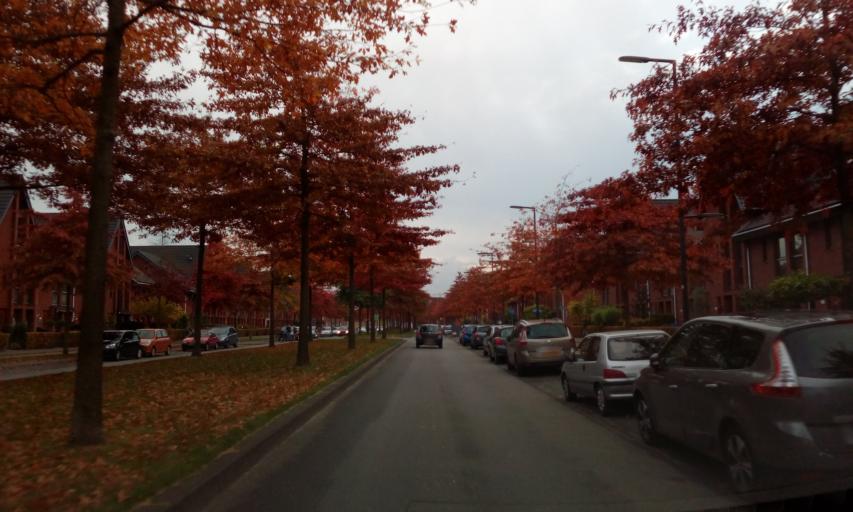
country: NL
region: South Holland
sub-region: Gemeente Capelle aan den IJssel
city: Capelle aan den IJssel
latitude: 51.9730
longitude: 4.5891
